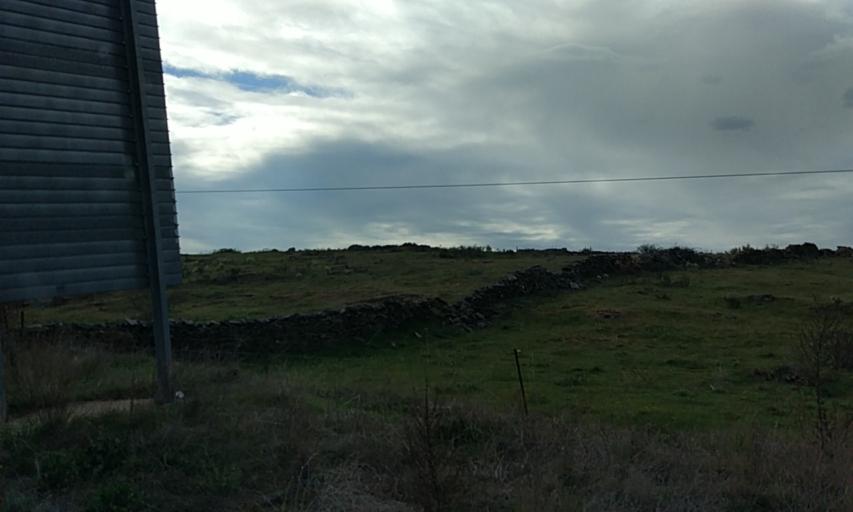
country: ES
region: Castille and Leon
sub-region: Provincia de Salamanca
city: Herguijuela de Ciudad Rodrigo
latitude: 40.4777
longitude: -6.5781
